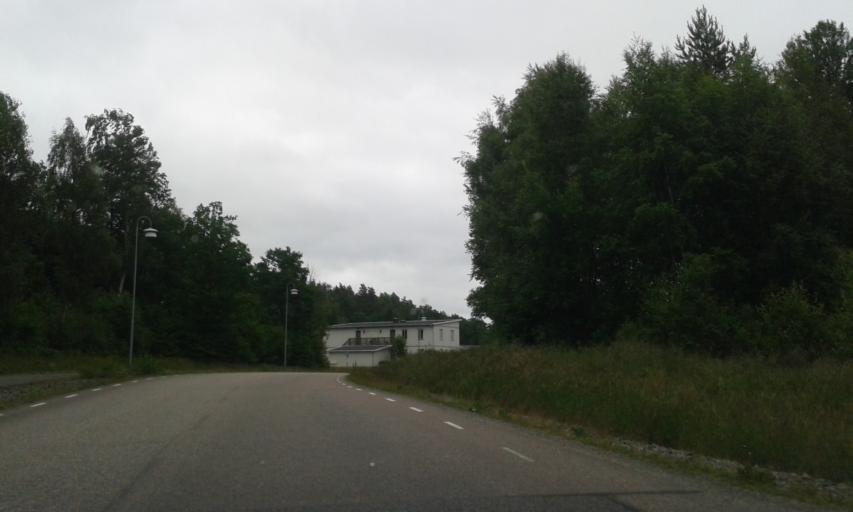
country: SE
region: Vaestra Goetaland
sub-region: Kungalvs Kommun
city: Kungalv
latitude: 57.8932
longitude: 11.9502
